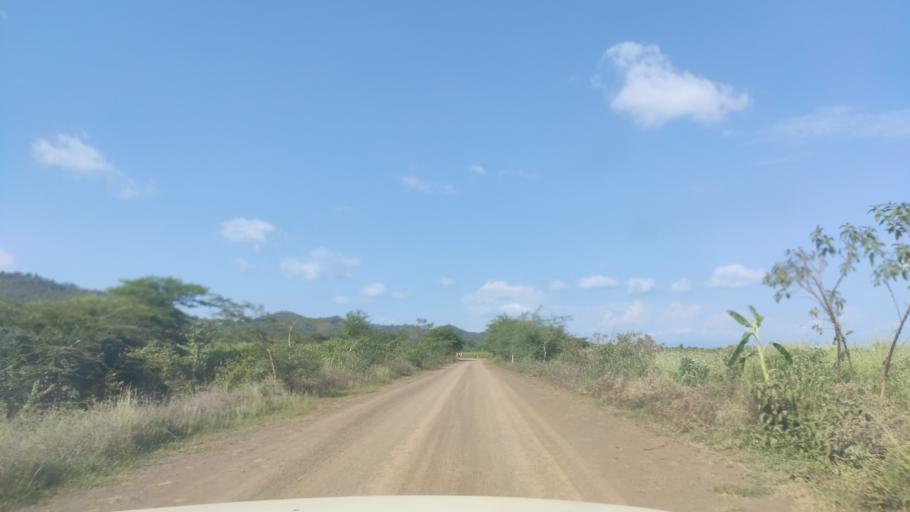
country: ET
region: Southern Nations, Nationalities, and People's Region
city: Felege Neway
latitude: 6.3929
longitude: 37.1001
